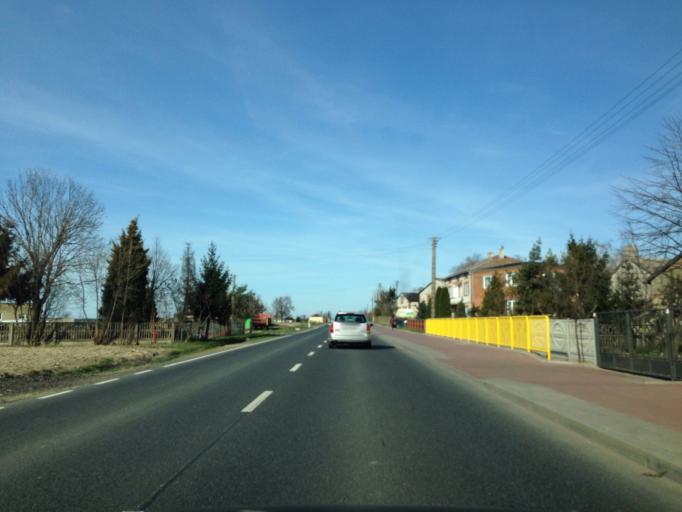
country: PL
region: Lodz Voivodeship
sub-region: Powiat poddebicki
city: Wartkowice
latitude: 51.9833
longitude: 19.0307
